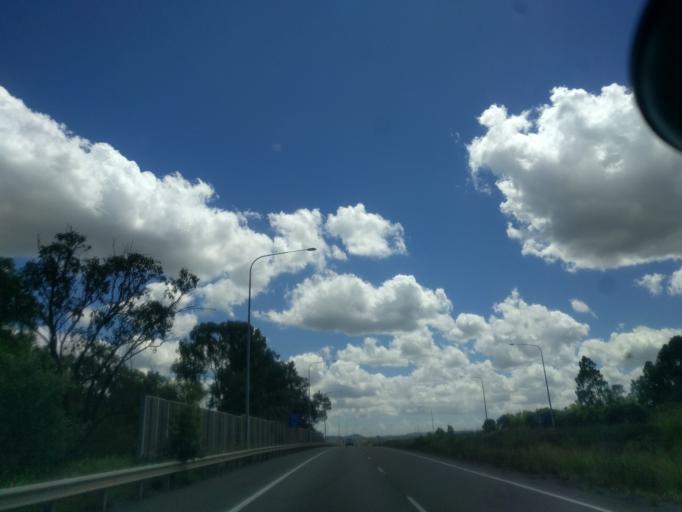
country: AU
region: Queensland
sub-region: Ipswich
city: Riverview
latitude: -27.6005
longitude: 152.8328
